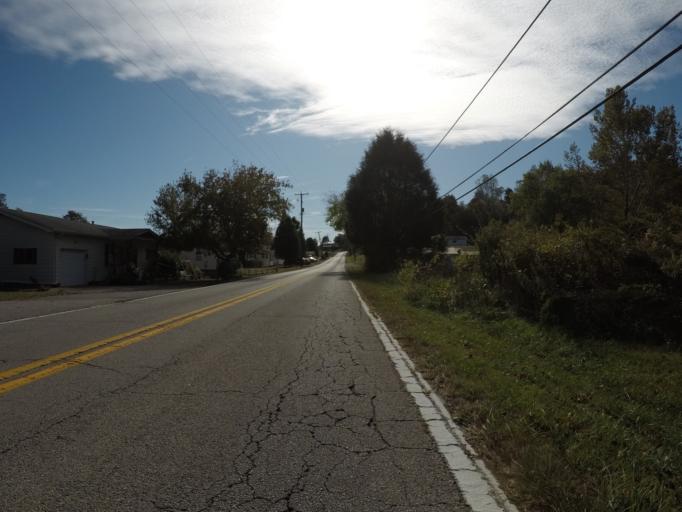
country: US
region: Ohio
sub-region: Lawrence County
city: Burlington
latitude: 38.3604
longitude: -82.5273
